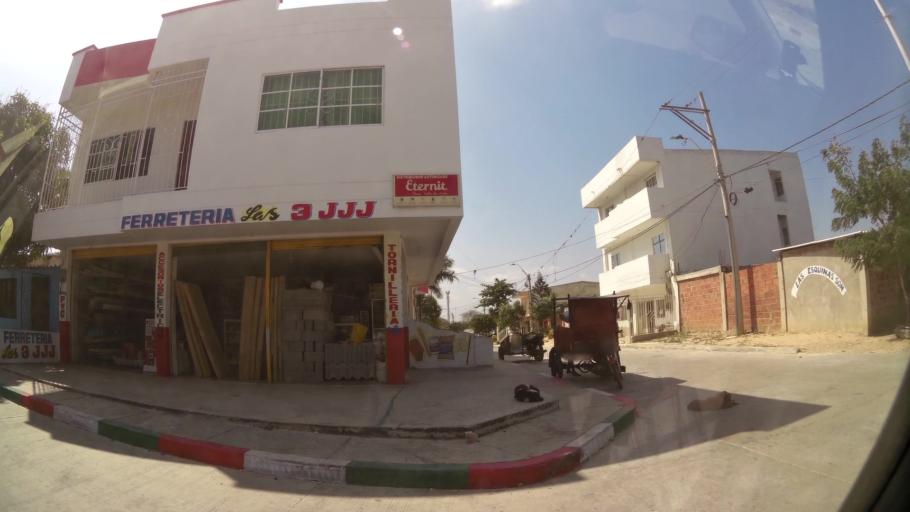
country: CO
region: Atlantico
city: Barranquilla
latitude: 10.9628
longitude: -74.8231
